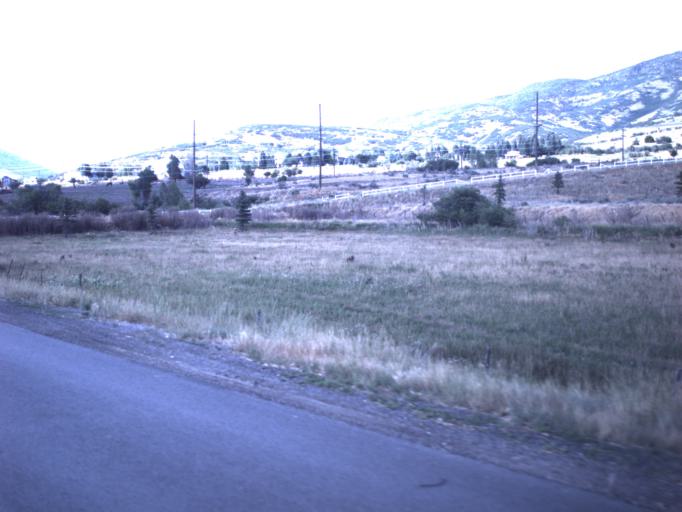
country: US
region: Utah
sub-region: Wasatch County
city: Heber
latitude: 40.5462
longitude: -111.4188
